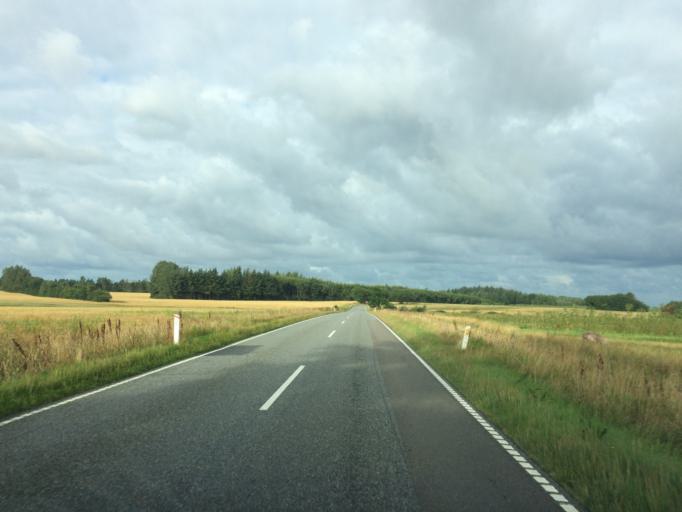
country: DK
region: Central Jutland
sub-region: Holstebro Kommune
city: Ulfborg
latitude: 56.1948
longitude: 8.3500
